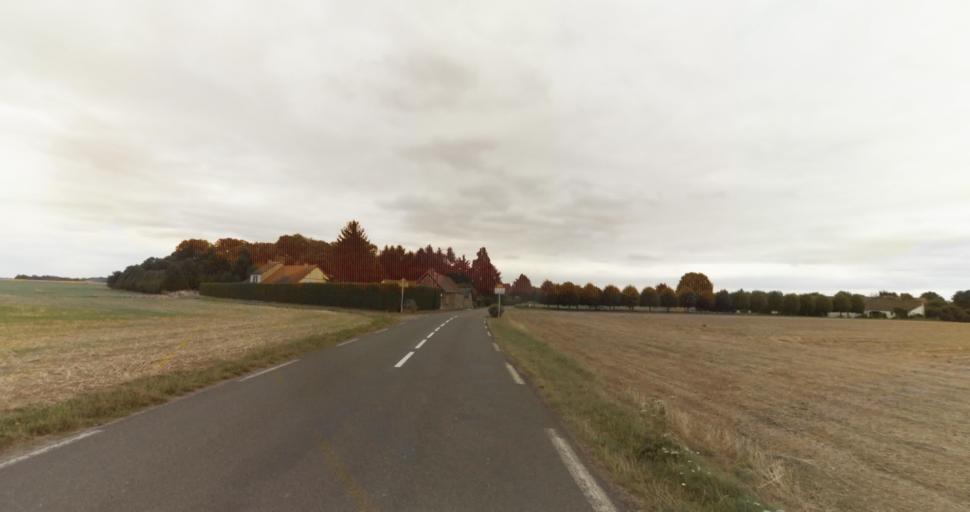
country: FR
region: Haute-Normandie
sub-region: Departement de l'Eure
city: Gravigny
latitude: 49.0050
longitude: 1.2312
